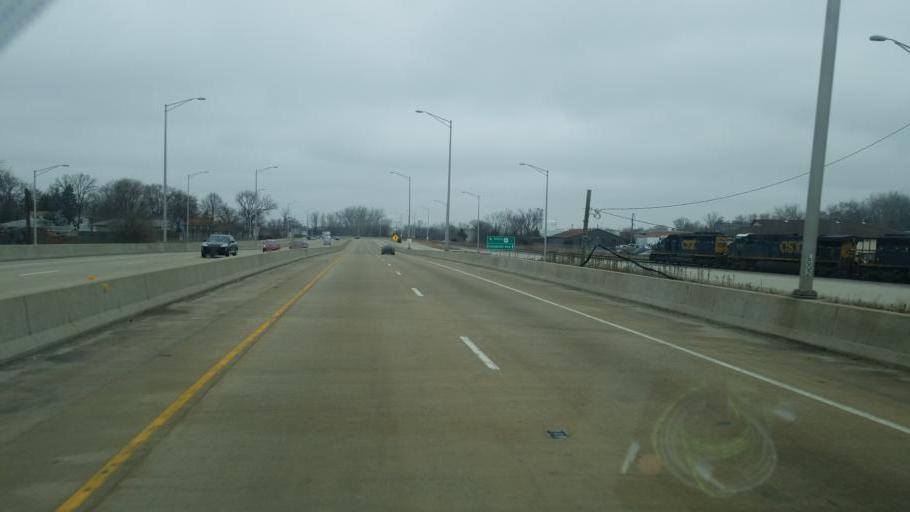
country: US
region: Illinois
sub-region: Lake County
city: Gurnee
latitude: 42.3709
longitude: -87.8961
